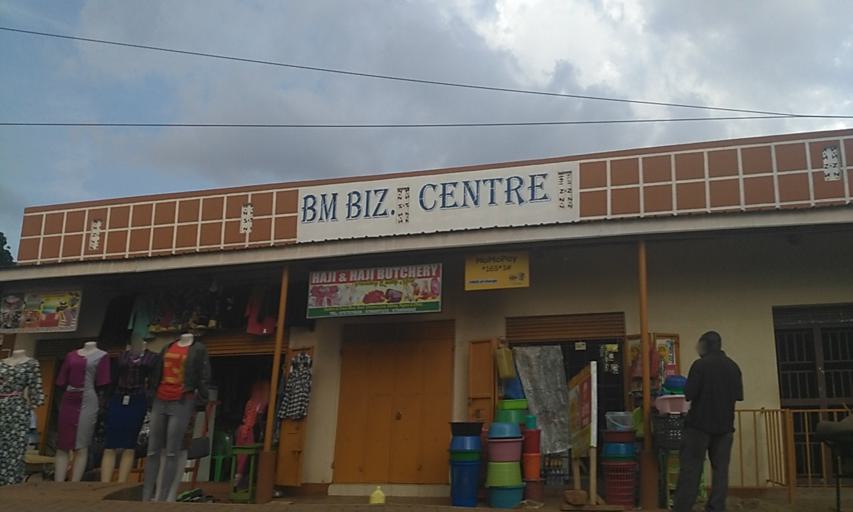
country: UG
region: Central Region
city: Kampala Central Division
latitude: 0.3306
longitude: 32.5575
